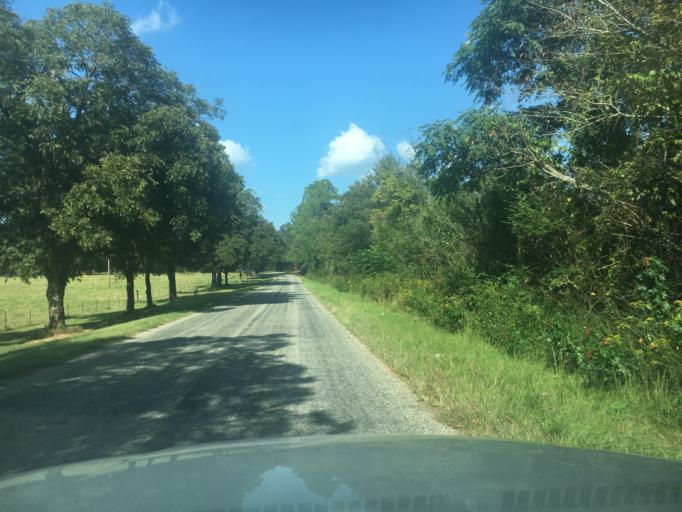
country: US
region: South Carolina
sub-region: Greenwood County
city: Ware Shoals
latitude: 34.4677
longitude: -82.2420
